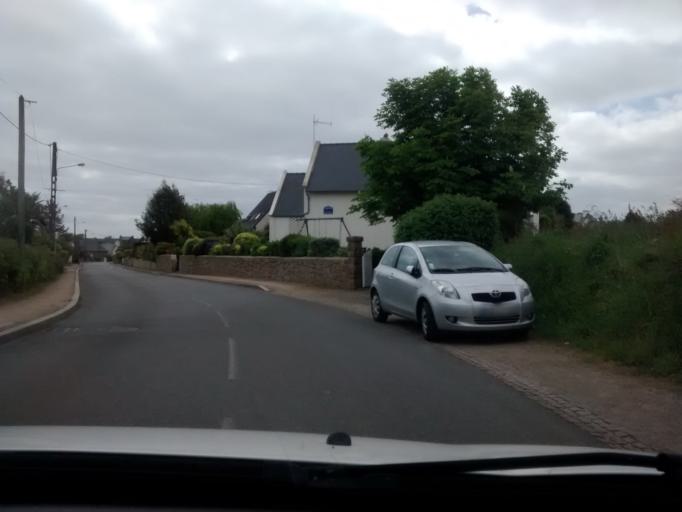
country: FR
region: Brittany
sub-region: Departement des Cotes-d'Armor
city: Tregastel
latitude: 48.8155
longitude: -3.4713
